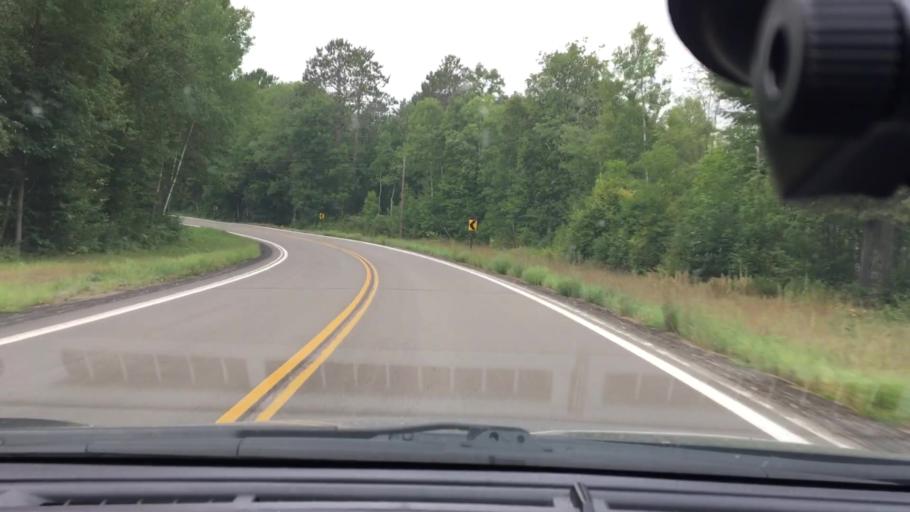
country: US
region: Minnesota
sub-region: Crow Wing County
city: Cross Lake
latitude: 46.6621
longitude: -93.9624
